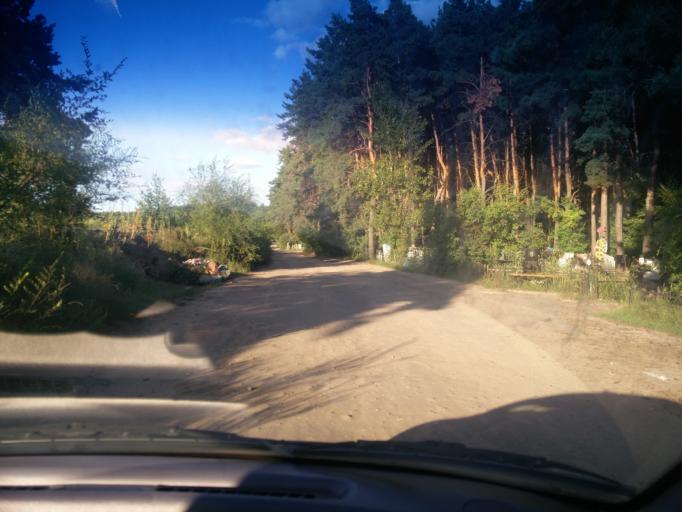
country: RU
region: Voronezj
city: Pridonskoy
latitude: 51.6699
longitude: 39.1030
